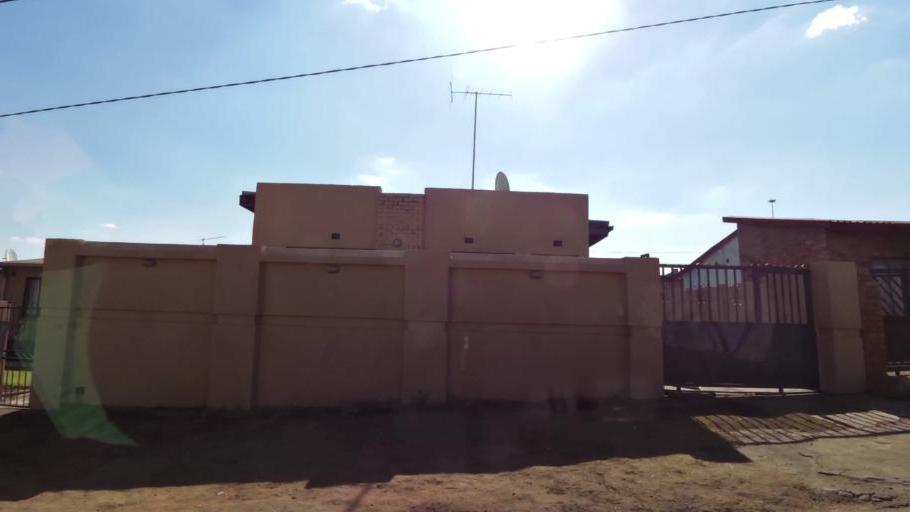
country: ZA
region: Gauteng
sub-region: City of Johannesburg Metropolitan Municipality
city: Soweto
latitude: -26.2395
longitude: 27.8918
